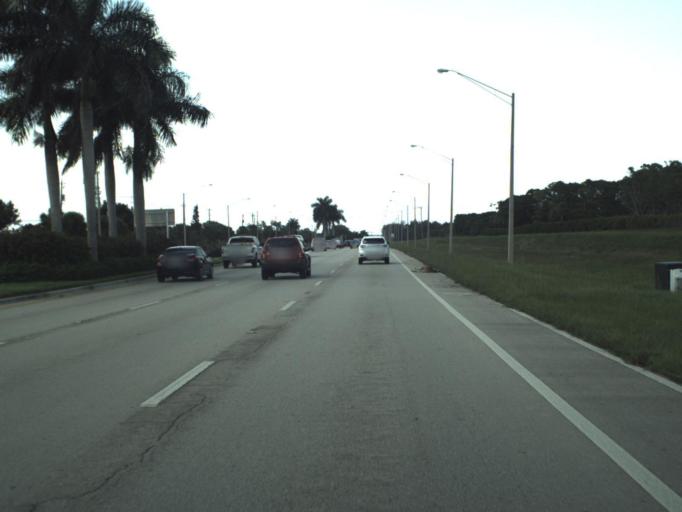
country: US
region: Florida
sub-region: Palm Beach County
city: Royal Palm Beach
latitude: 26.6939
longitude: -80.2014
